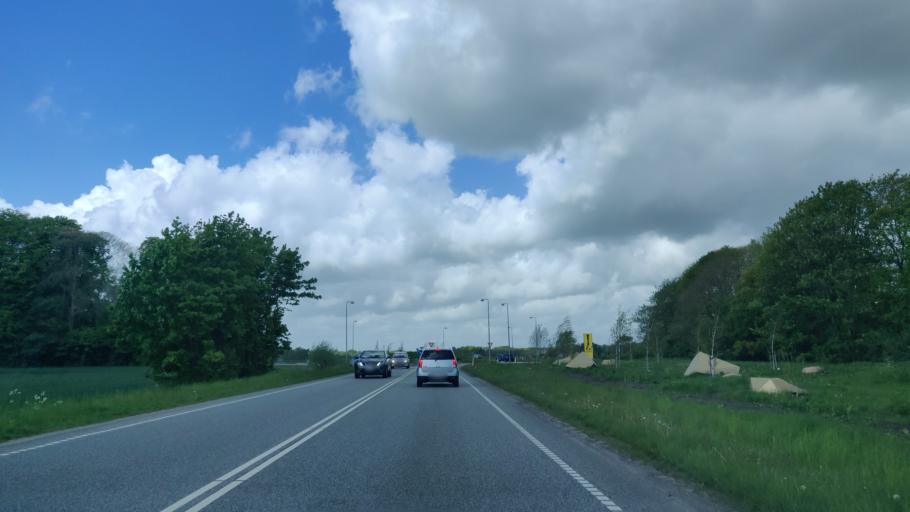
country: DK
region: Central Jutland
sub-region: Hedensted Kommune
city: Torring
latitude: 55.8475
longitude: 9.4777
